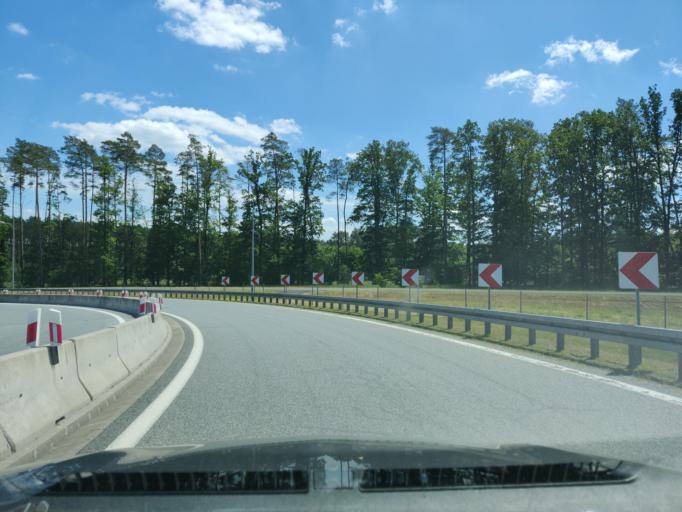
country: PL
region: Greater Poland Voivodeship
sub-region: Powiat nowotomyski
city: Nowy Tomysl
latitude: 52.3581
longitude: 16.1014
